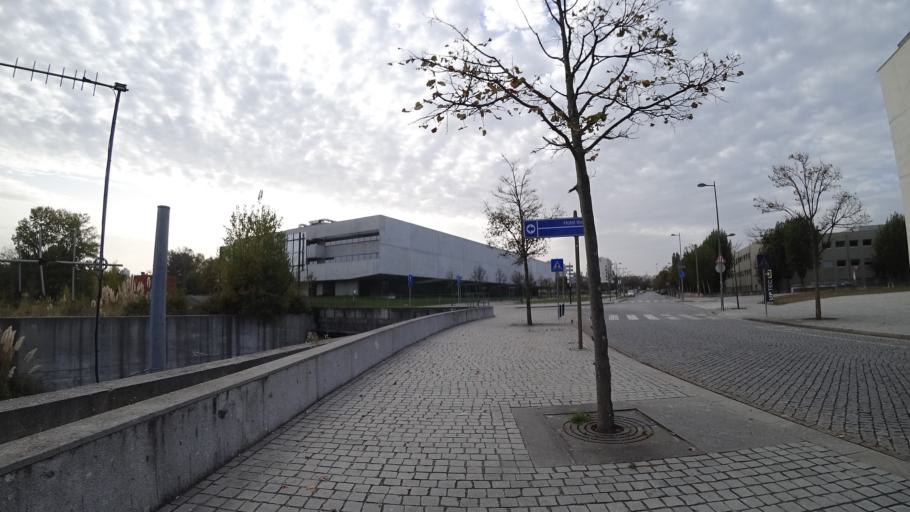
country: PT
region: Porto
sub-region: Matosinhos
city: Sao Mamede de Infesta
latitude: 41.1768
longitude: -8.6040
